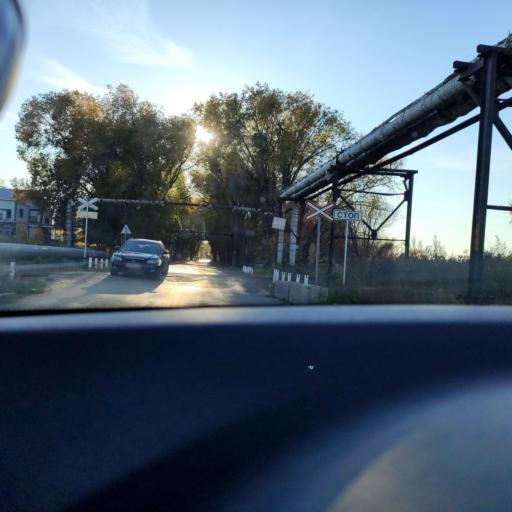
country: RU
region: Samara
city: Smyshlyayevka
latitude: 53.1917
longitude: 50.2946
